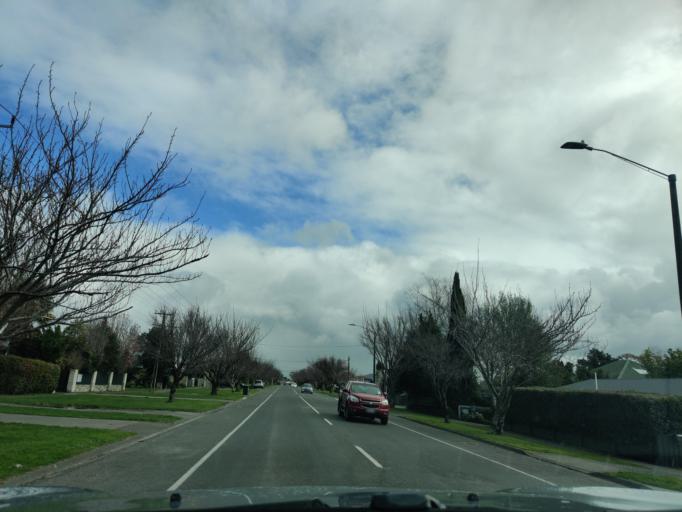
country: NZ
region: Hawke's Bay
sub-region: Hastings District
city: Hastings
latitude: -39.6710
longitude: 176.8727
